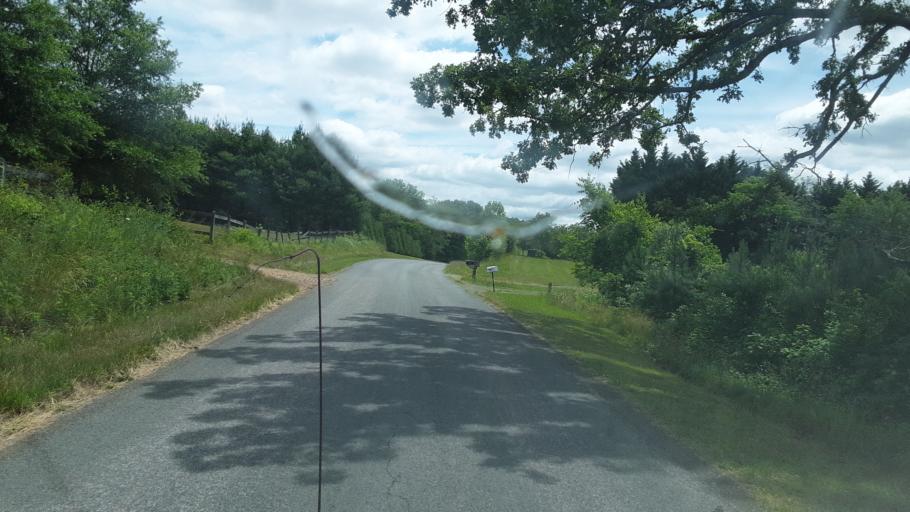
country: US
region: Virginia
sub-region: Pittsylvania County
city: Chatham
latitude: 36.8458
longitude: -79.4216
